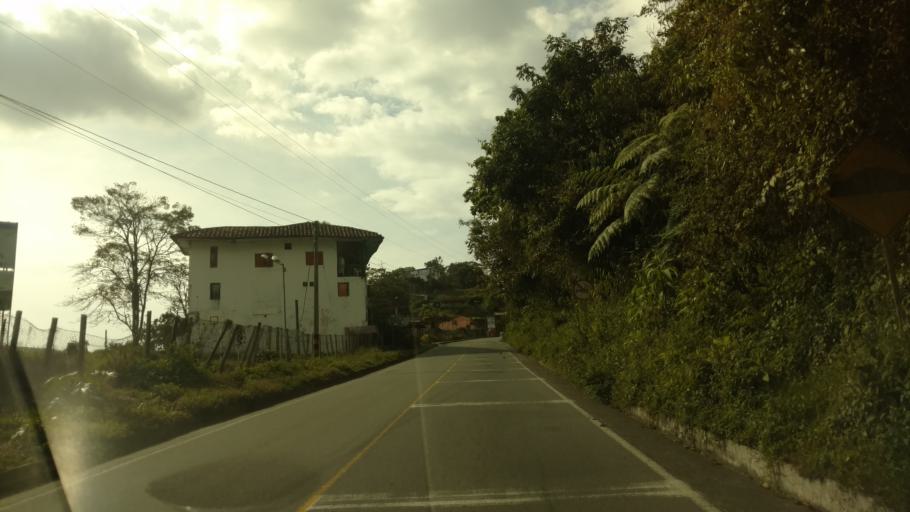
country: CO
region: Caldas
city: Neira
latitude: 5.1562
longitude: -75.5126
